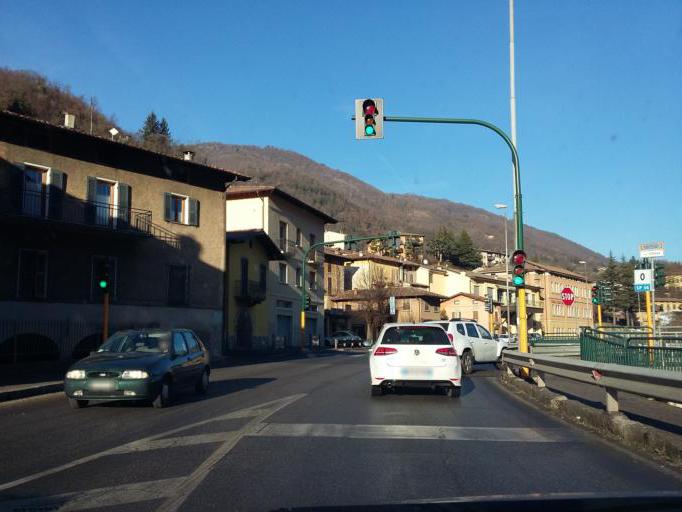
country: IT
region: Lombardy
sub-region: Provincia di Brescia
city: Vestone
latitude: 45.7103
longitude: 10.4055
